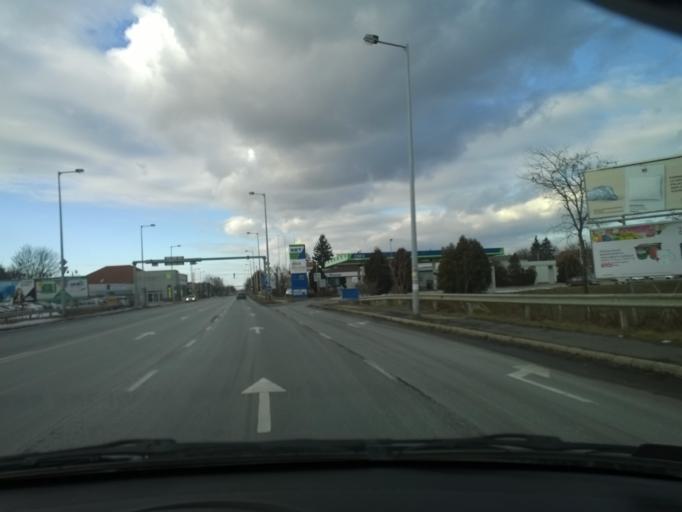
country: HU
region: Fejer
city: Szekesfehervar
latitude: 47.1962
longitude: 18.4447
